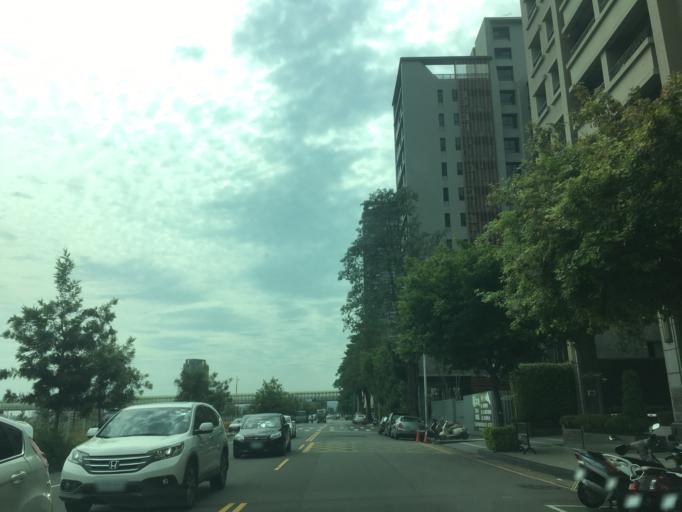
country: TW
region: Taiwan
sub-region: Taichung City
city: Taichung
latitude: 24.1294
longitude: 120.6497
